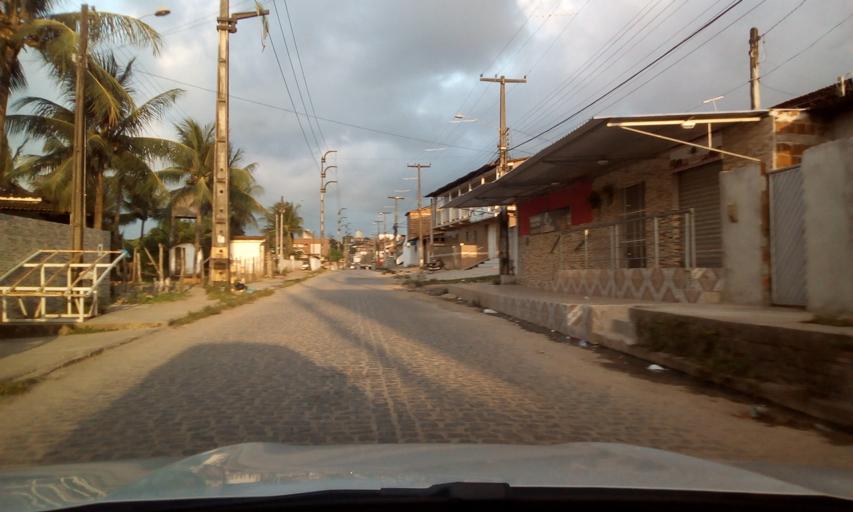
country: BR
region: Paraiba
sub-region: Bayeux
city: Bayeux
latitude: -7.1842
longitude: -34.8906
